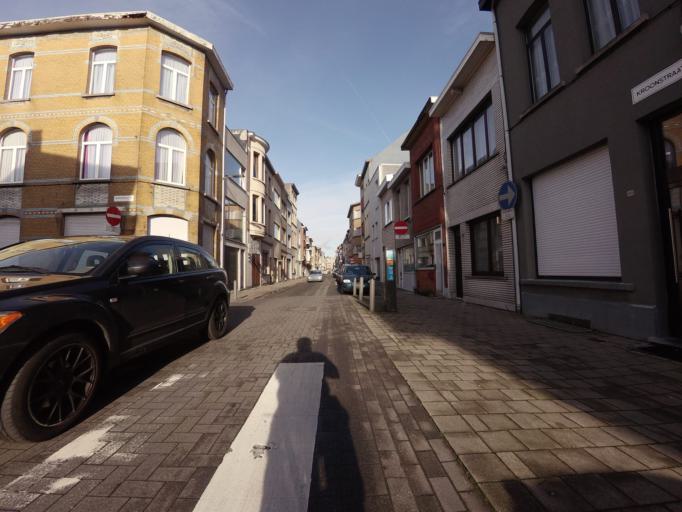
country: BE
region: Flanders
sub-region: Provincie Antwerpen
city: Antwerpen
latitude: 51.2130
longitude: 4.4295
